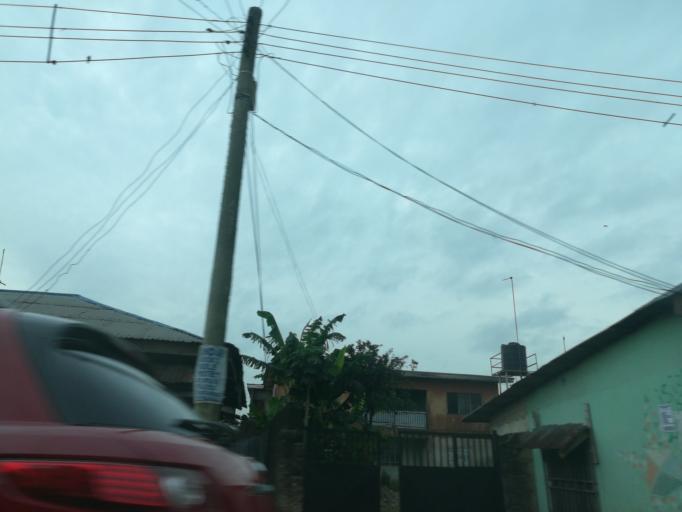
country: NG
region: Rivers
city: Port Harcourt
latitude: 4.8339
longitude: 7.0238
